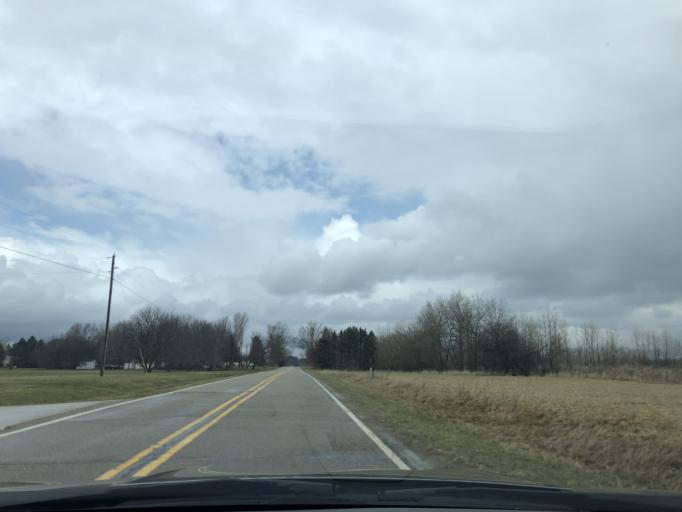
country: US
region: Michigan
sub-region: Clinton County
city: Saint Johns
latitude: 43.0477
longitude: -84.6015
